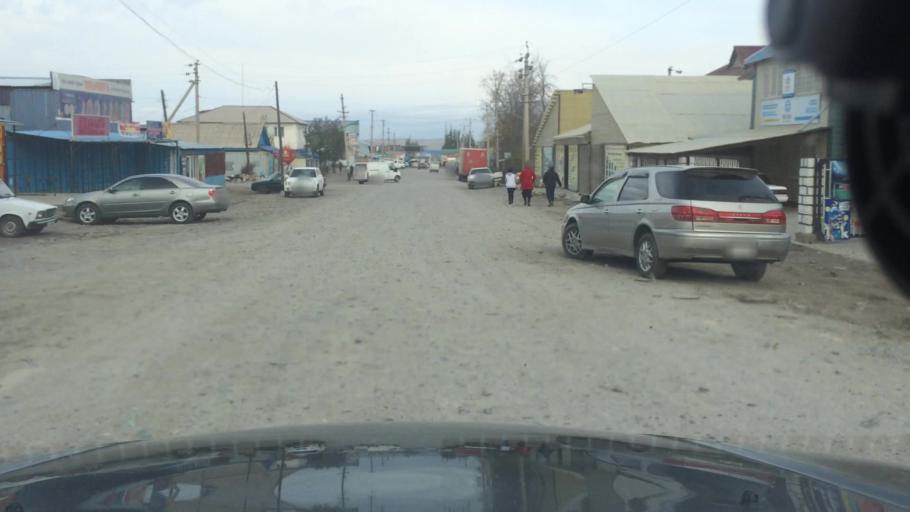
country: KG
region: Ysyk-Koel
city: Karakol
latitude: 42.4905
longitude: 78.3875
